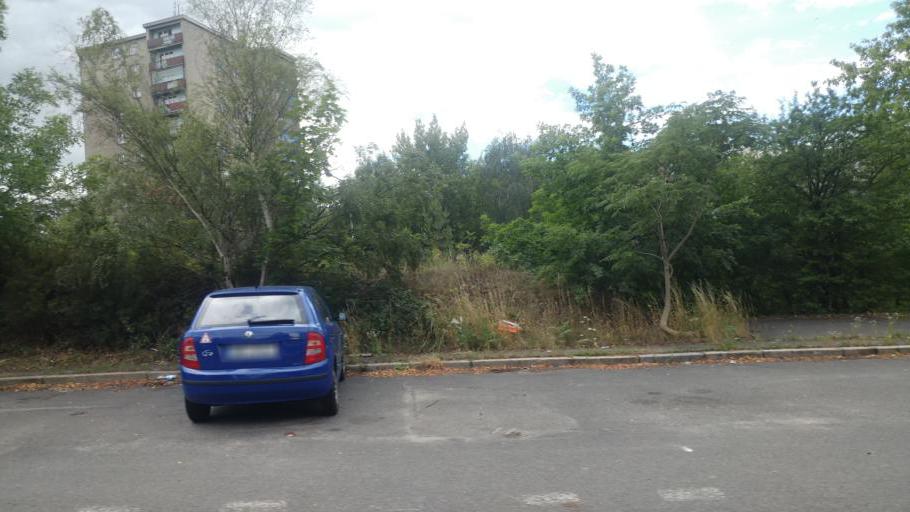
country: CZ
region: Praha
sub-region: Praha 8
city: Karlin
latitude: 50.0475
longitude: 14.4842
